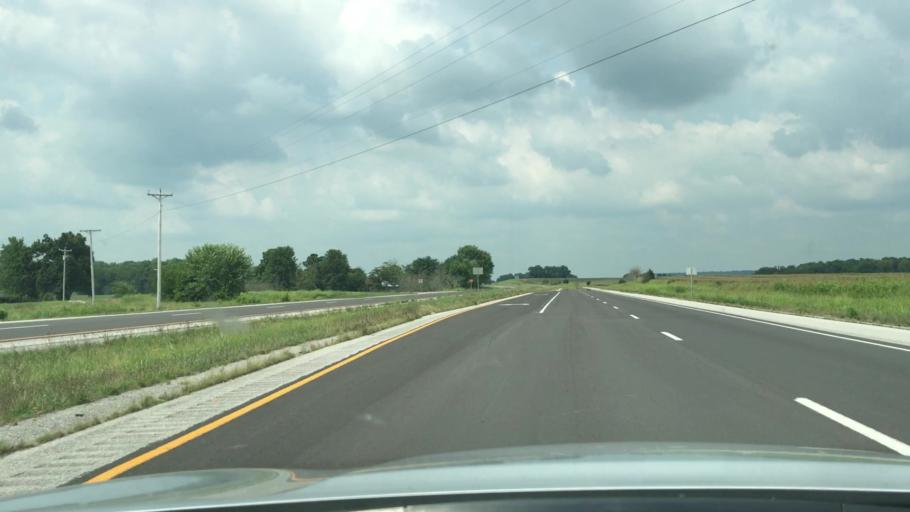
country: US
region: Kentucky
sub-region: Todd County
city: Elkton
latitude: 36.8127
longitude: -87.0291
